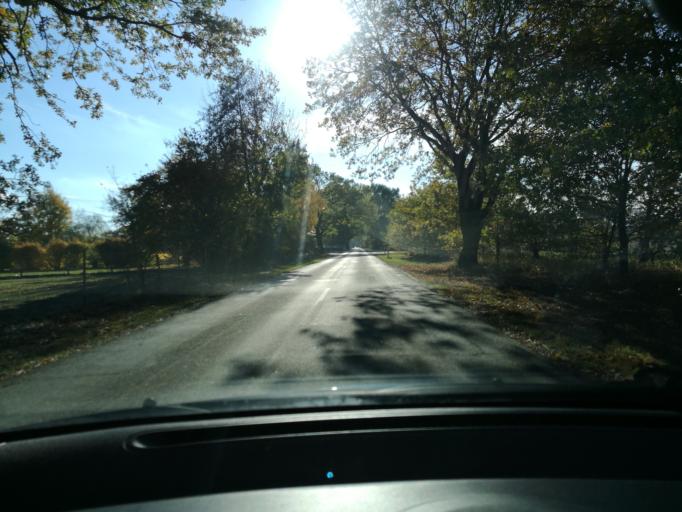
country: DE
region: Mecklenburg-Vorpommern
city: Neu Kaliss
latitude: 53.1383
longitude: 11.3212
